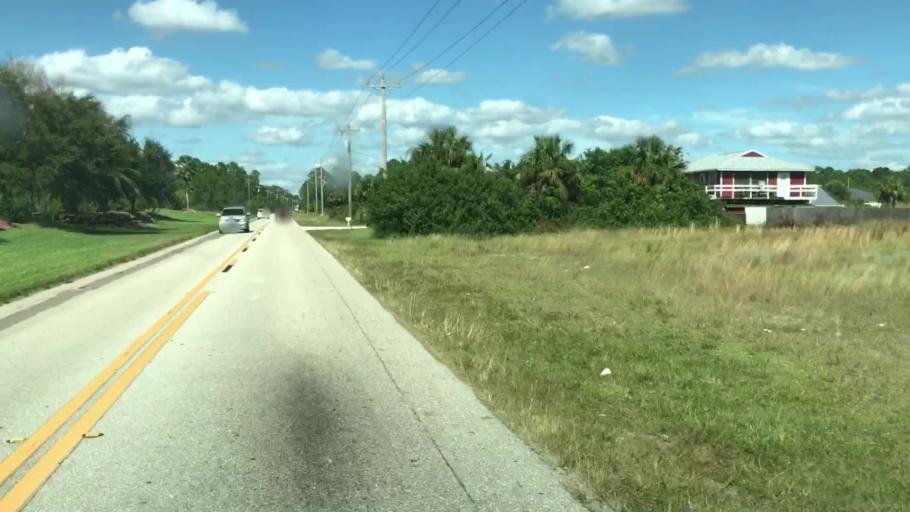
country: US
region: Florida
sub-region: Lee County
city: Lehigh Acres
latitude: 26.6257
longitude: -81.6463
